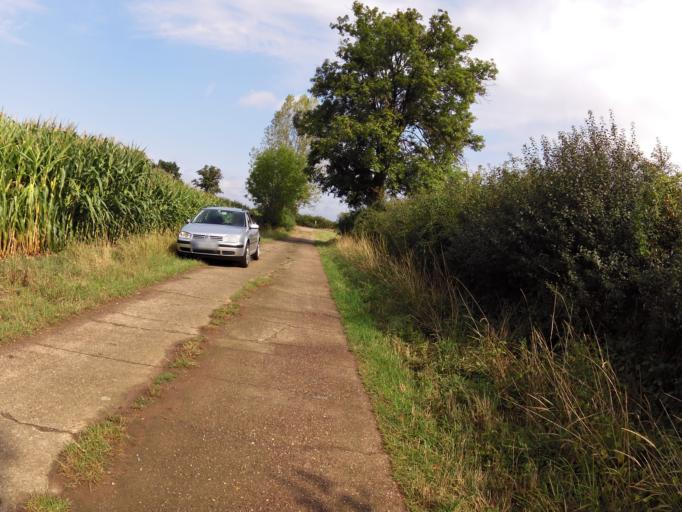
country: DE
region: Lower Saxony
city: Drakenburg
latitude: 52.7034
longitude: 9.1929
